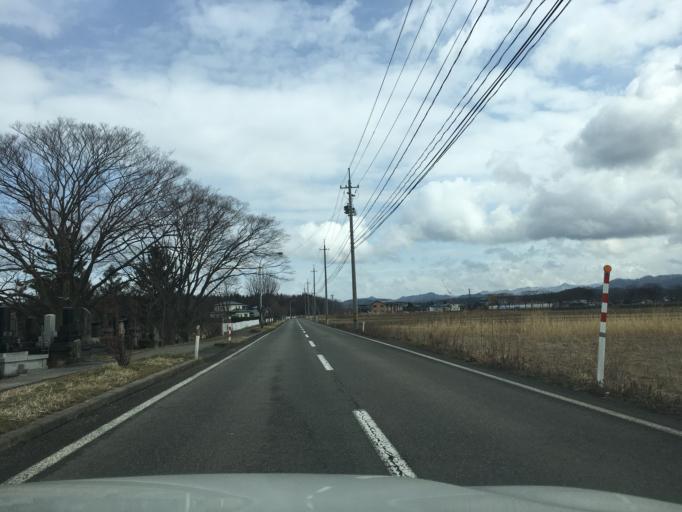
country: JP
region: Akita
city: Tenno
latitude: 39.9378
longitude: 140.1071
